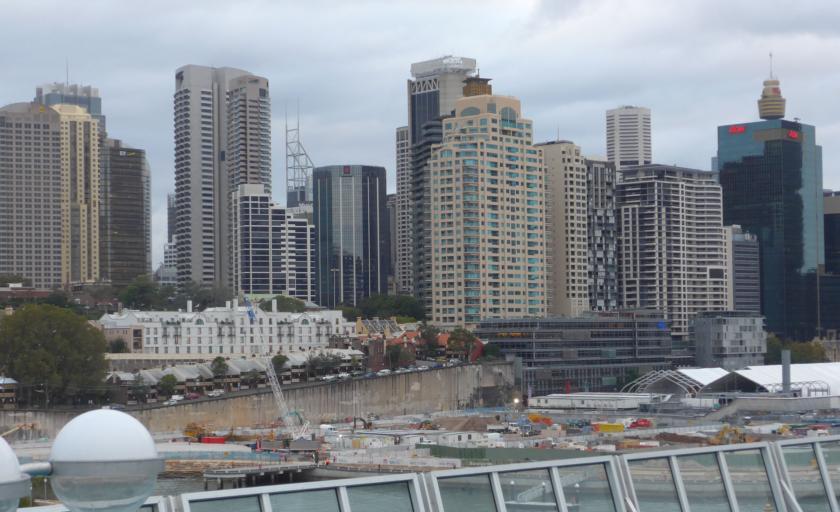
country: AU
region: New South Wales
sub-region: Leichhardt
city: Balmain East
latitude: -33.8570
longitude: 151.1985
